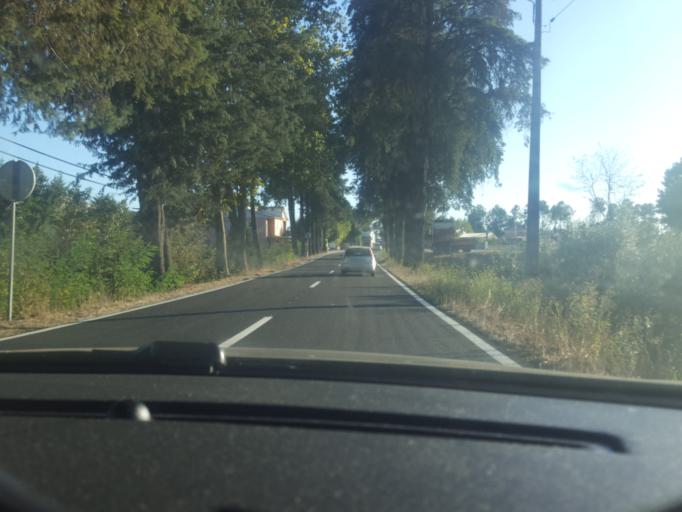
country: PT
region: Viseu
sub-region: Mangualde
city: Mangualde
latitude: 40.5871
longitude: -7.8029
